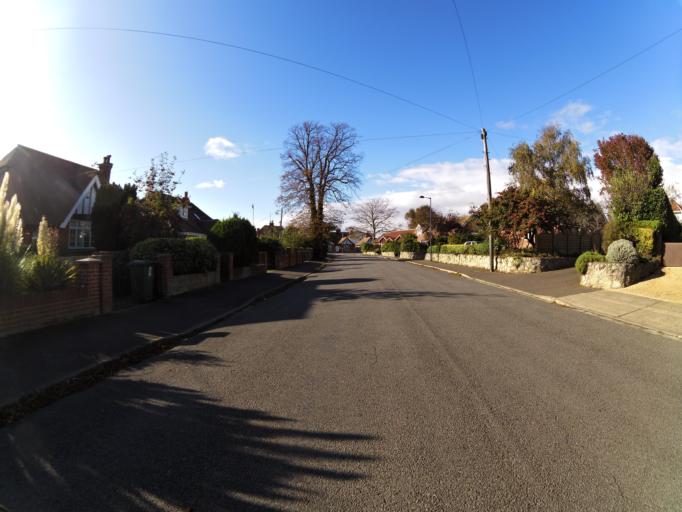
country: GB
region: England
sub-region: Suffolk
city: Felixstowe
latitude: 51.9670
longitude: 1.3570
